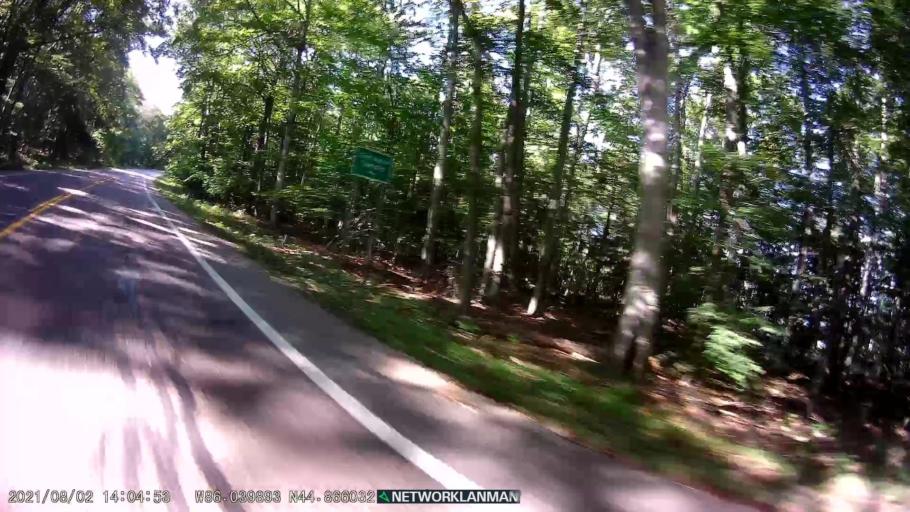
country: US
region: Michigan
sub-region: Benzie County
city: Beulah
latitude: 44.8661
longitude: -86.0400
